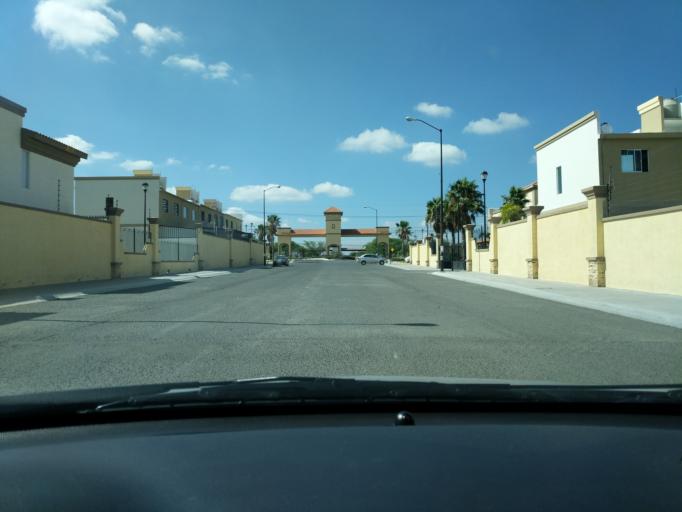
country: MX
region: Queretaro
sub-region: Queretaro
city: Patria Nueva
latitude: 20.6461
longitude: -100.4854
